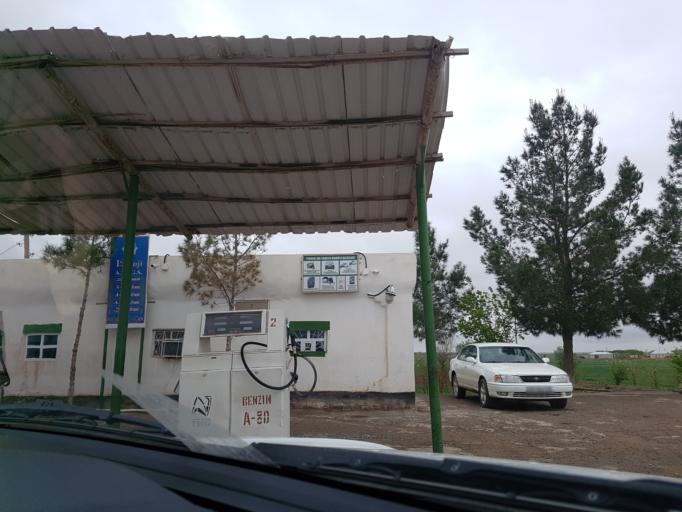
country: TM
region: Lebap
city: Sayat
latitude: 38.4359
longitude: 64.3886
